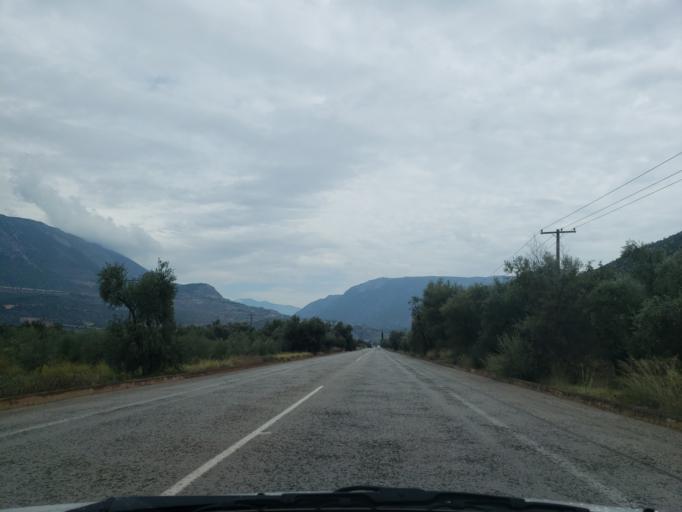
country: GR
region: Central Greece
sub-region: Nomos Fokidos
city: Itea
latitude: 38.4831
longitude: 22.4266
